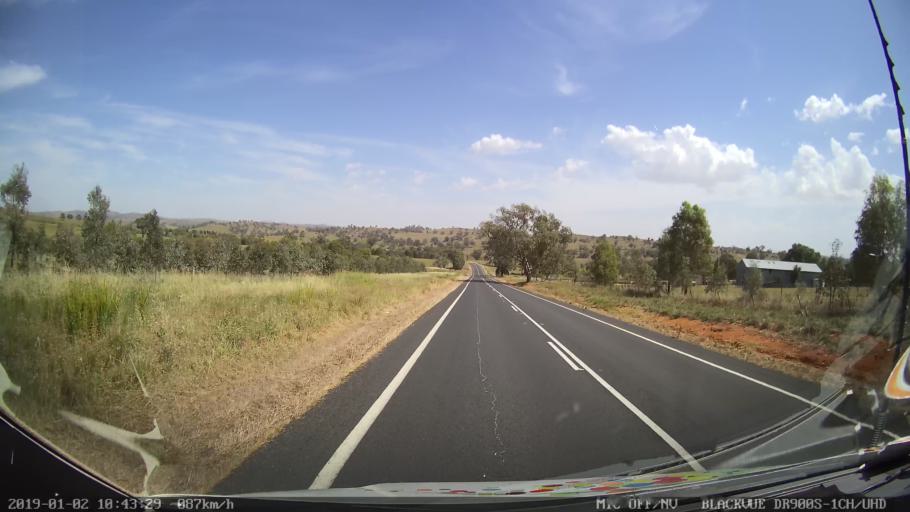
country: AU
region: New South Wales
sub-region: Cootamundra
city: Cootamundra
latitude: -34.7720
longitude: 148.3038
